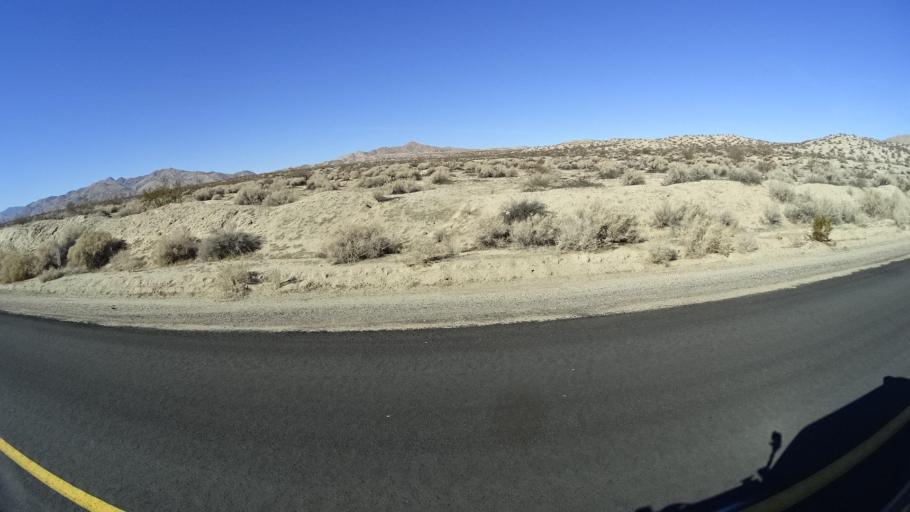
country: US
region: California
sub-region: Kern County
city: California City
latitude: 35.3156
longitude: -117.9630
